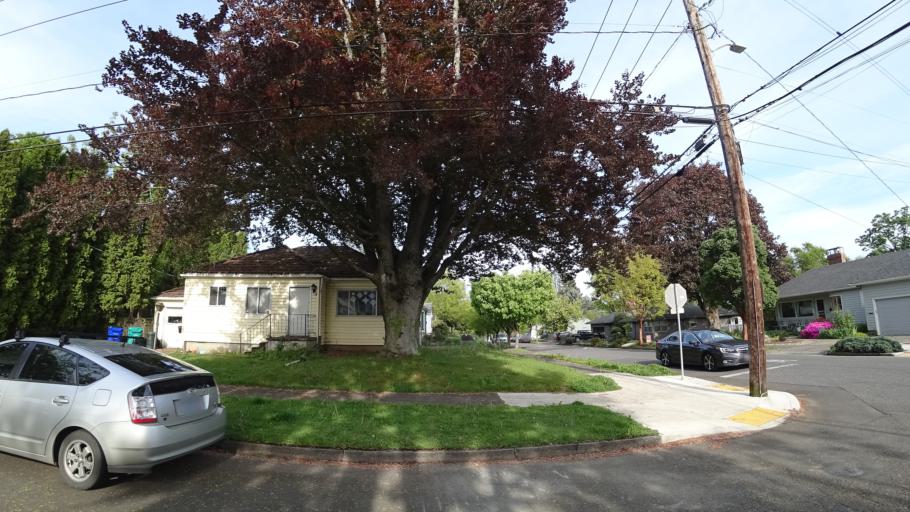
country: US
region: Oregon
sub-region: Clackamas County
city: Milwaukie
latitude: 45.4651
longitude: -122.6195
